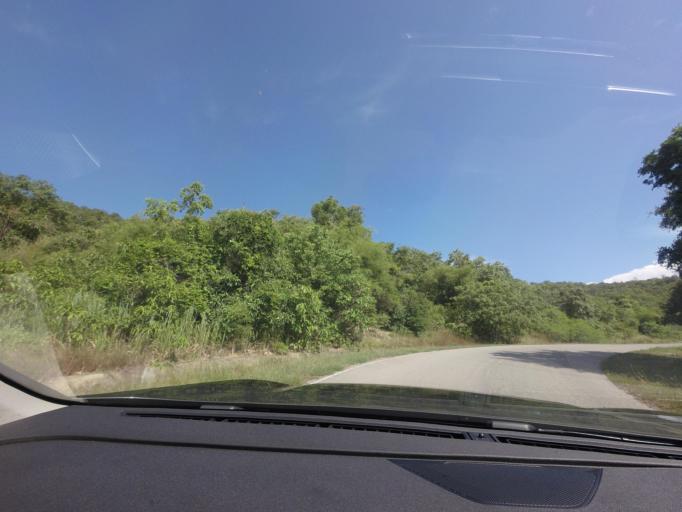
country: TH
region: Prachuap Khiri Khan
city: Hua Hin
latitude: 12.4973
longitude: 99.9471
